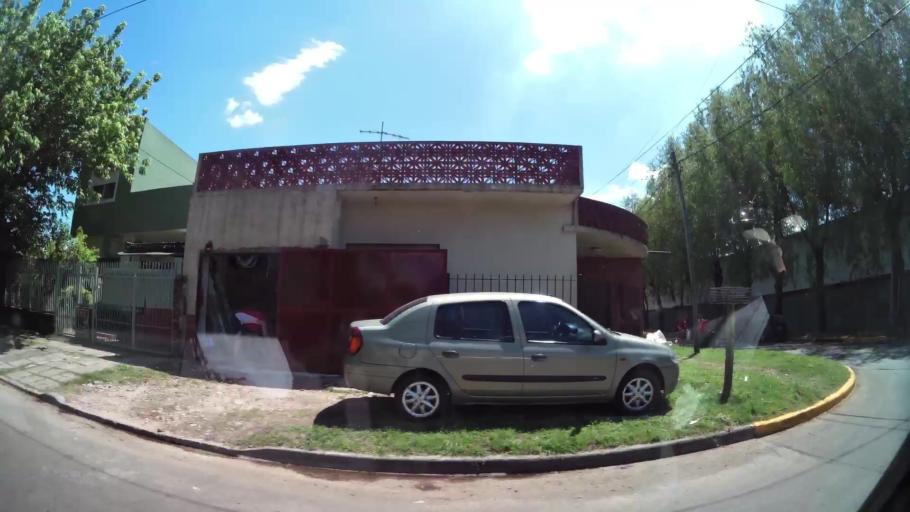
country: AR
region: Buenos Aires
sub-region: Partido de Tigre
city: Tigre
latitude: -34.4336
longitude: -58.5790
